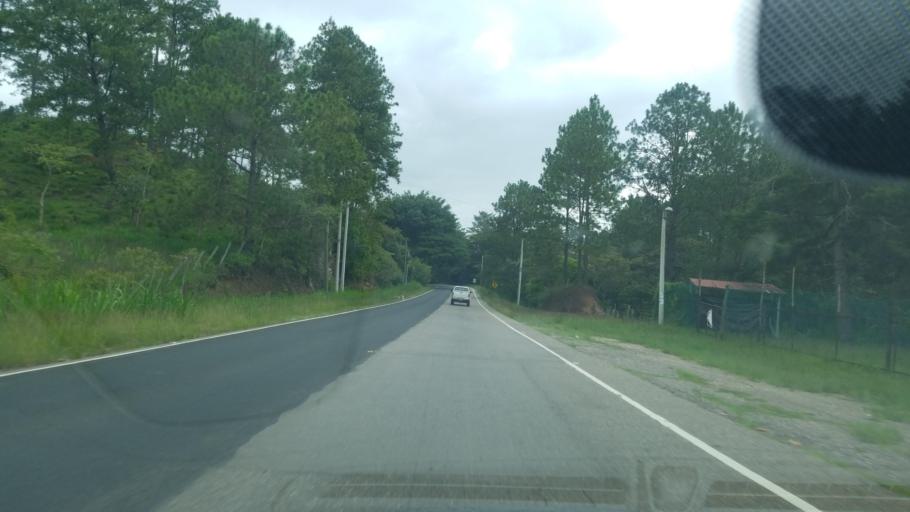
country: HN
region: Ocotepeque
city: Sinuapa
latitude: 14.4579
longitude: -89.1520
